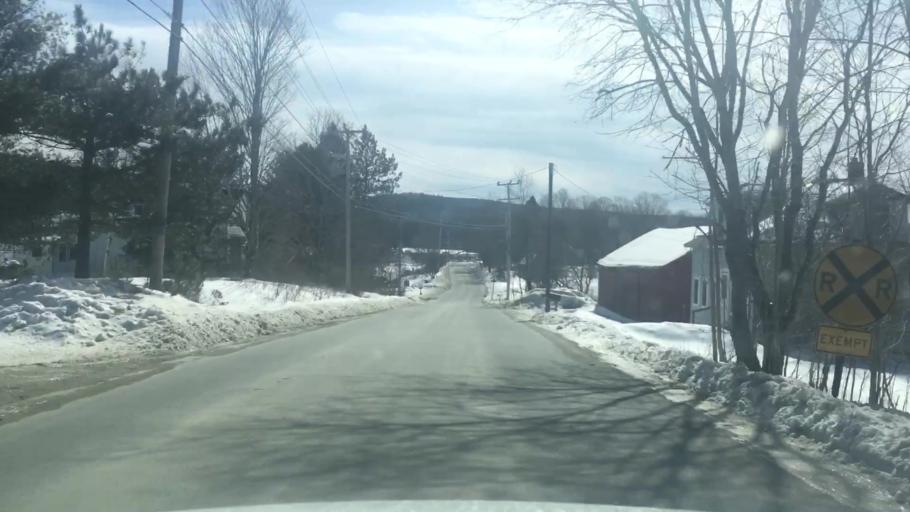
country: US
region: Maine
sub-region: Penobscot County
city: Holden
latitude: 44.7407
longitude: -68.6290
